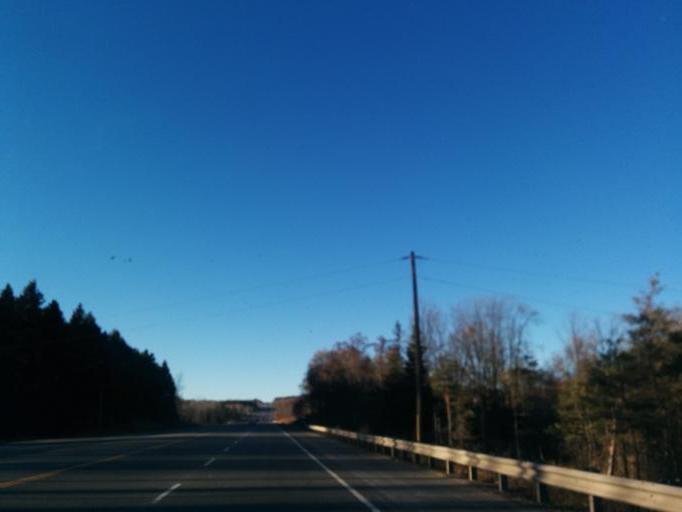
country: CA
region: Ontario
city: Orangeville
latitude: 43.8252
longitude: -79.9482
